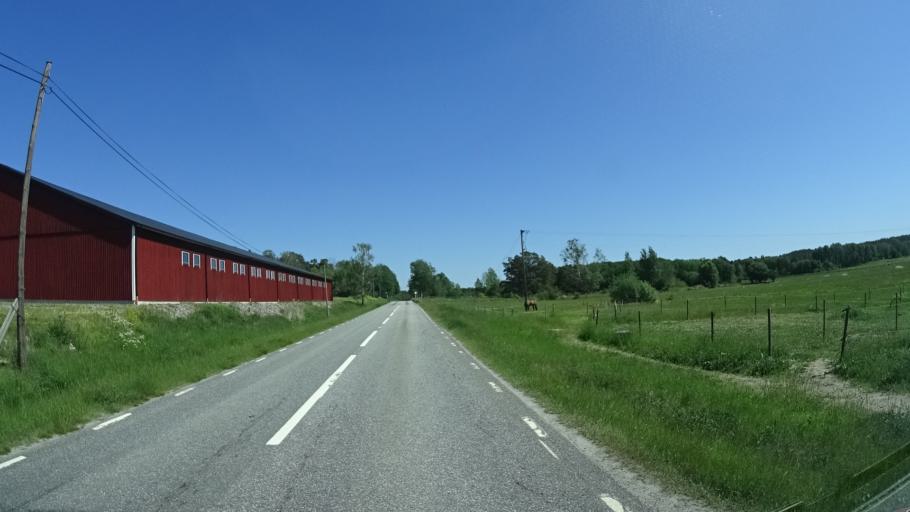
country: SE
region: Stockholm
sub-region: Vallentuna Kommun
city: Vallentuna
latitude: 59.5957
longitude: 18.1099
